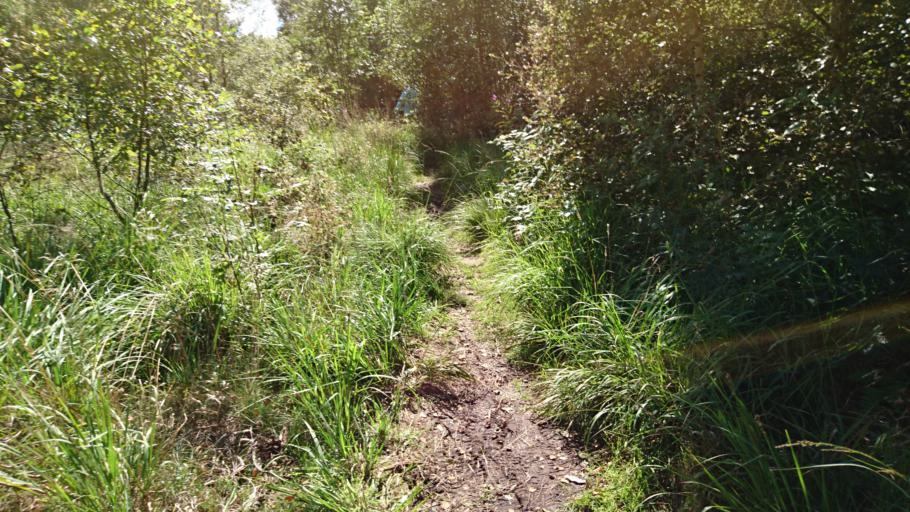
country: DK
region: North Denmark
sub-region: Alborg Kommune
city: Storvorde
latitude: 56.8696
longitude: 10.1806
